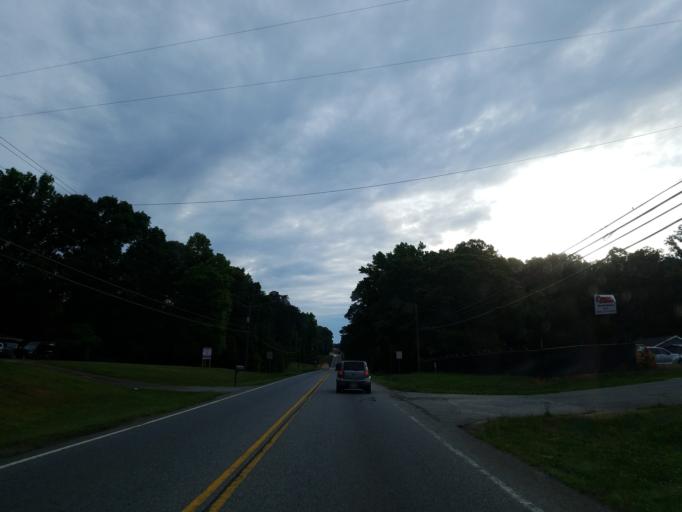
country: US
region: Georgia
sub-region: Forsyth County
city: Cumming
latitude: 34.2324
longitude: -84.1688
